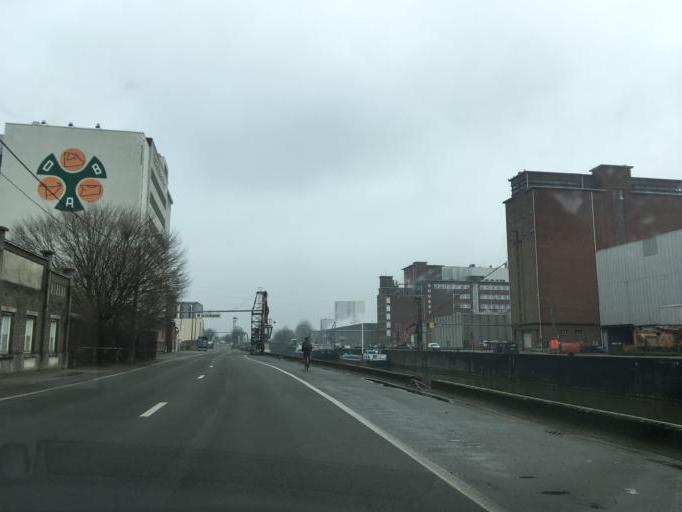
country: BE
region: Flanders
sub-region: Provincie West-Vlaanderen
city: Roeselare
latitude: 50.9428
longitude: 3.1406
